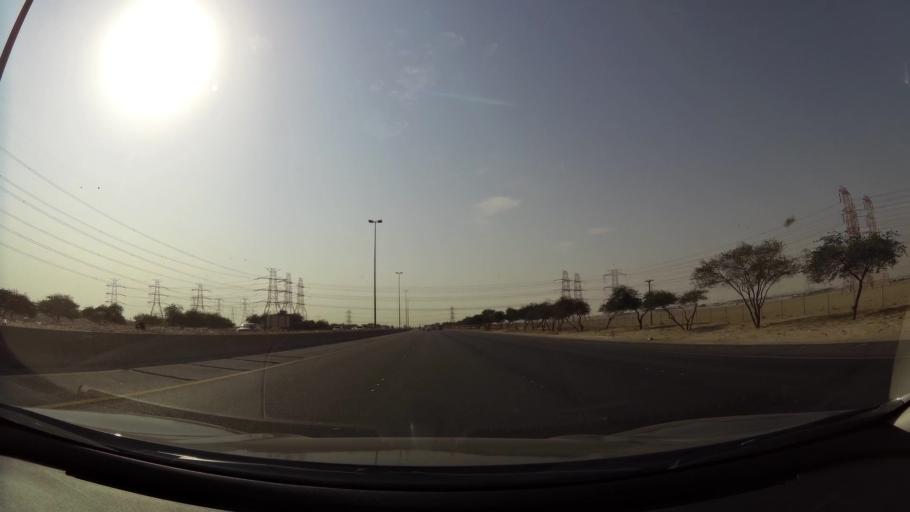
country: KW
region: Al Ahmadi
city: Al Ahmadi
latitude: 29.0151
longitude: 48.0925
